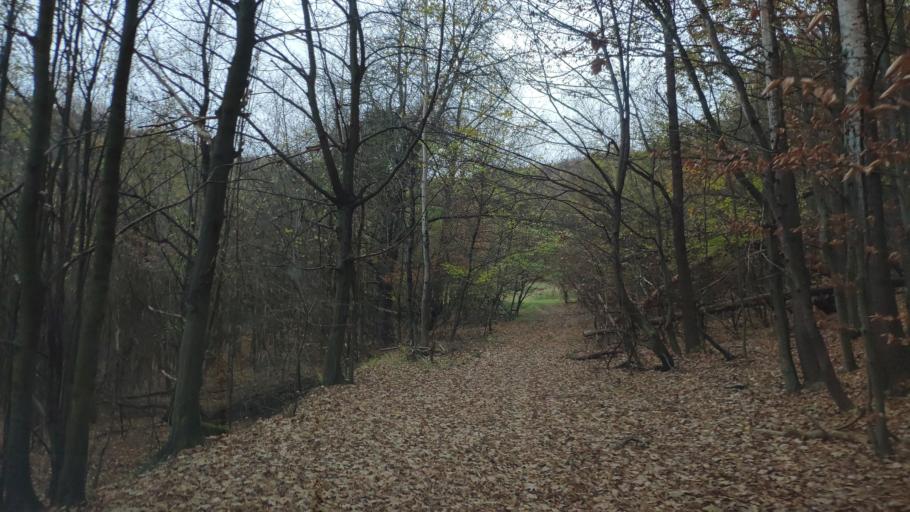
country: SK
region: Presovsky
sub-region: Okres Presov
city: Presov
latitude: 48.9408
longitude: 21.1384
